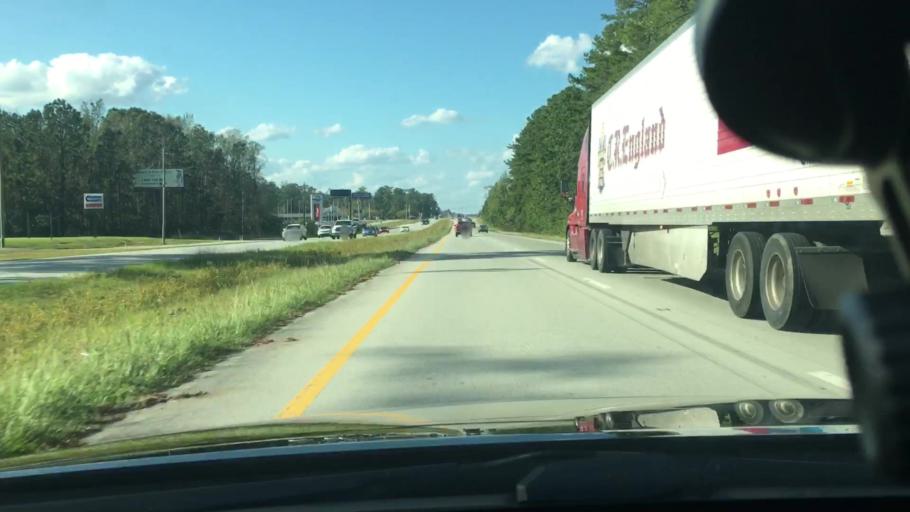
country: US
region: North Carolina
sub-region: Craven County
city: James City
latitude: 35.0460
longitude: -77.0118
